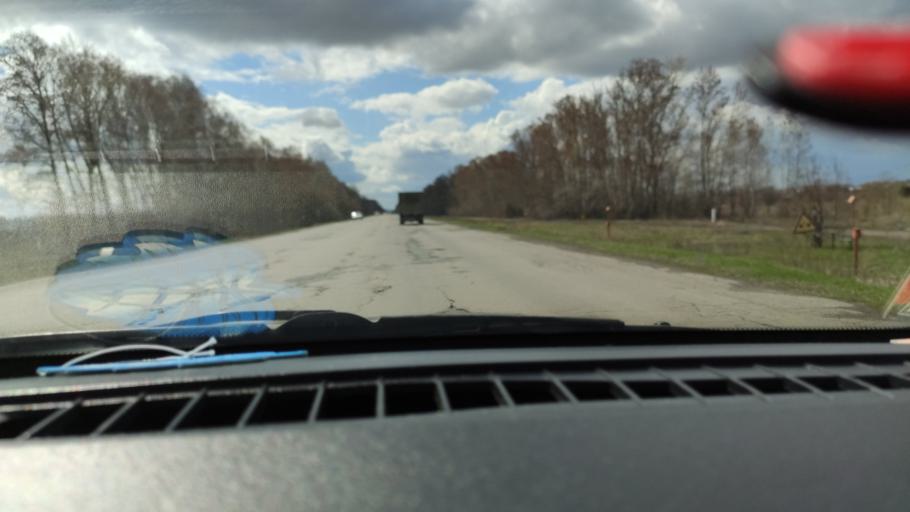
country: RU
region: Samara
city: Tol'yatti
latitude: 53.6342
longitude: 49.4183
